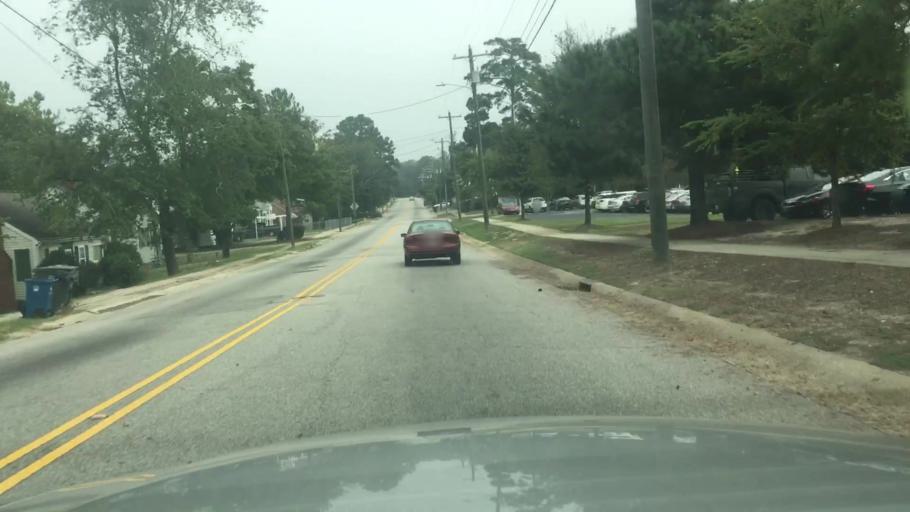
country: US
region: North Carolina
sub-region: Cumberland County
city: Fayetteville
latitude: 35.0728
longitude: -78.8834
